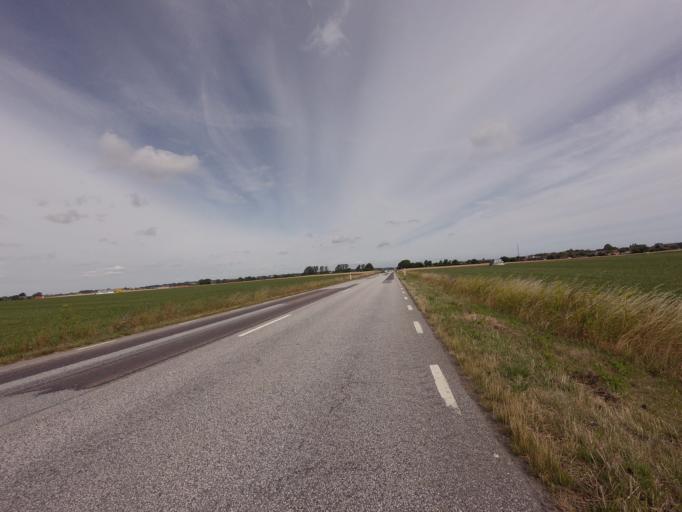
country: SE
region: Skane
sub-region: Simrishamns Kommun
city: Simrishamn
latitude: 55.5369
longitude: 14.3394
